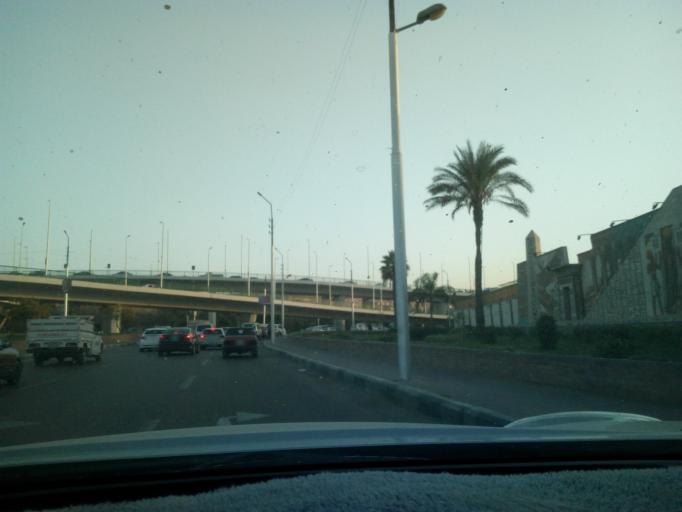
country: EG
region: Muhafazat al Qalyubiyah
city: Al Khankah
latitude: 30.1110
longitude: 31.3694
